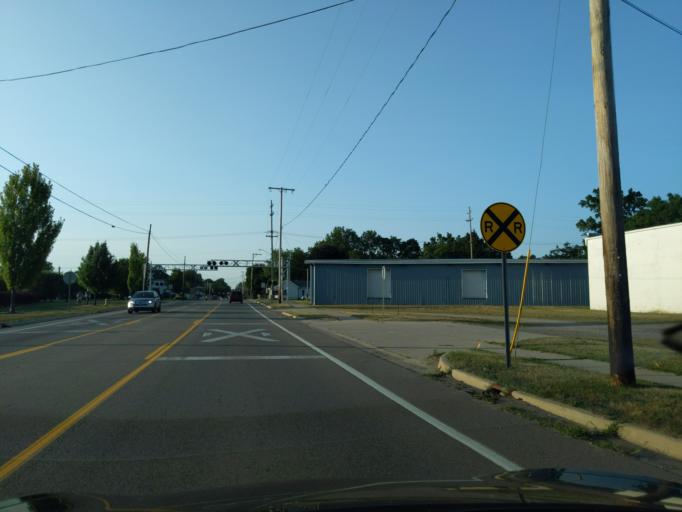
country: US
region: Michigan
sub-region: Shiawassee County
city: Owosso
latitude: 42.9937
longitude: -84.1768
